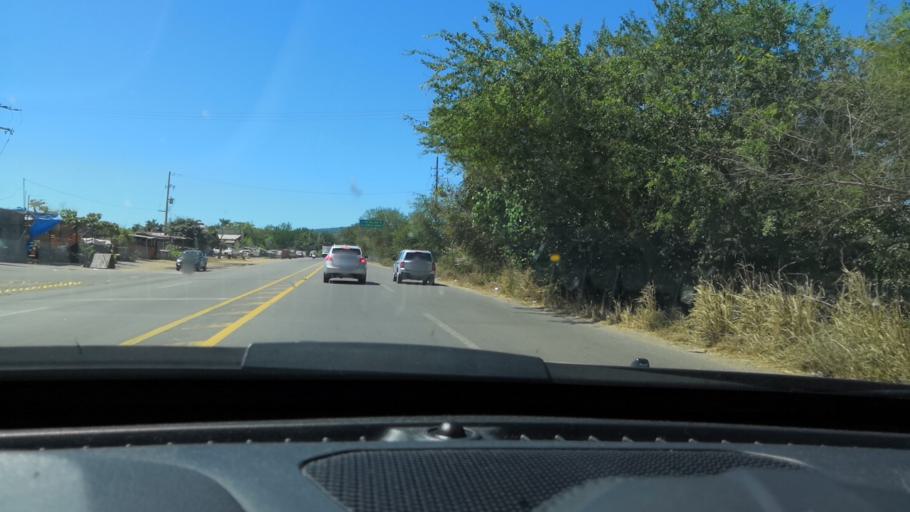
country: MX
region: Nayarit
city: Las Varas
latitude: 21.1735
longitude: -105.1460
